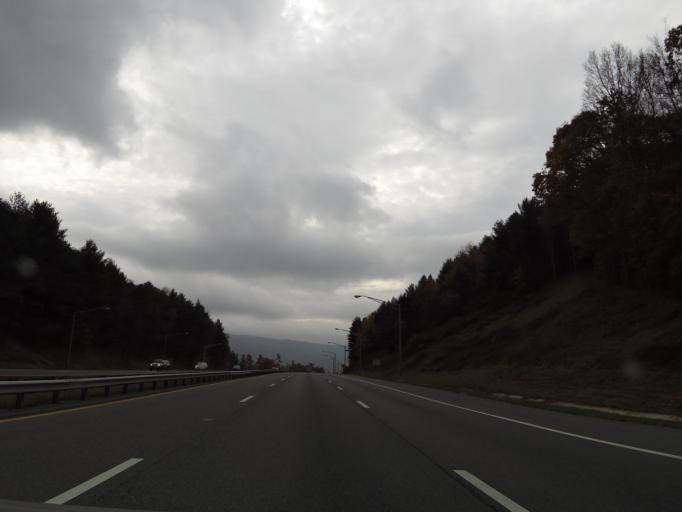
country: US
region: Virginia
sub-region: Bland County
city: Bland
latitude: 37.0900
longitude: -81.1275
